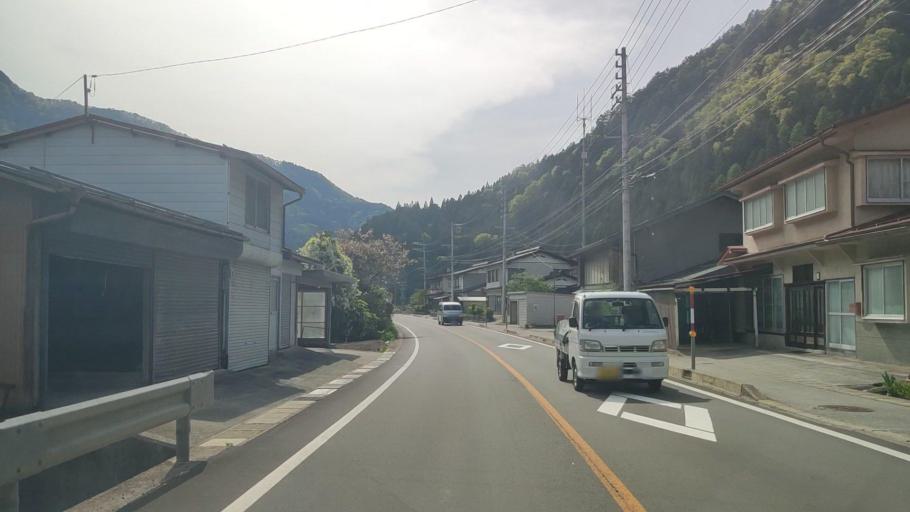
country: JP
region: Gifu
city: Takayama
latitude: 36.2497
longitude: 137.4942
